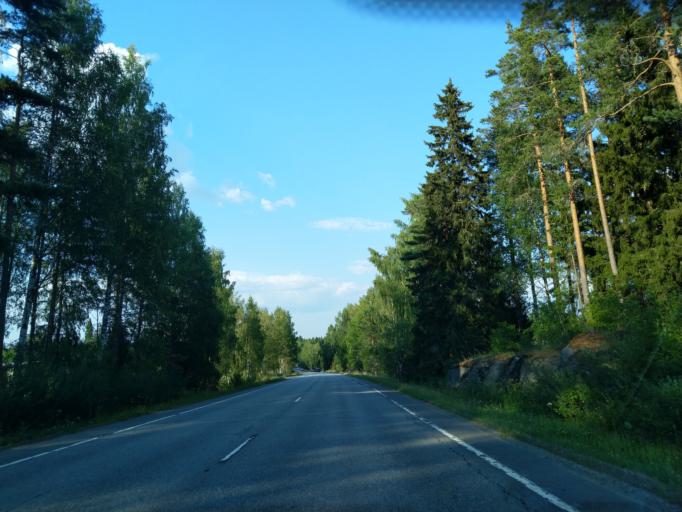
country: FI
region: Satakunta
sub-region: Pori
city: Laengelmaeki
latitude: 61.7550
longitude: 22.1284
